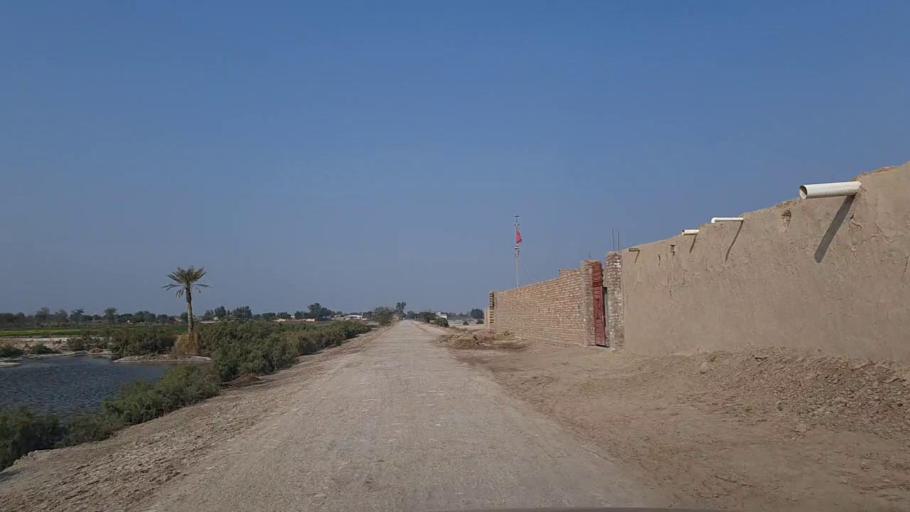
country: PK
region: Sindh
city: Daur
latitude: 26.4207
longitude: 68.4089
